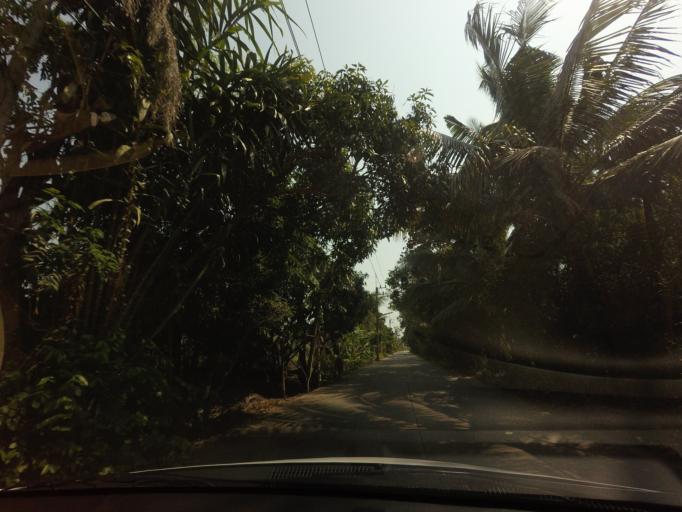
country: TH
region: Samut Sakhon
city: Krathum Baen
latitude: 13.6924
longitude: 100.2540
